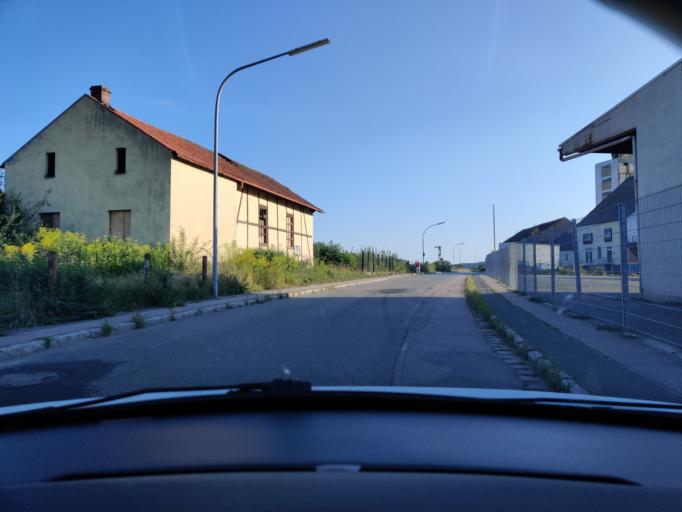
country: DE
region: Bavaria
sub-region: Upper Palatinate
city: Nabburg
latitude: 49.4496
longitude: 12.1823
